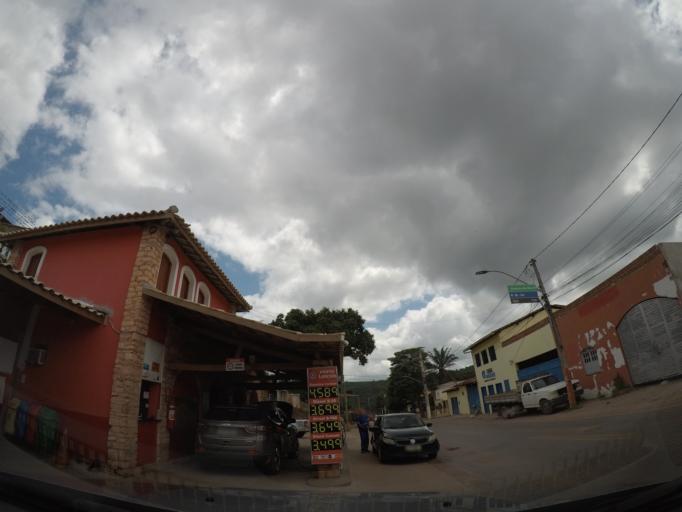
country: BR
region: Bahia
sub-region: Andarai
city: Vera Cruz
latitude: -12.5606
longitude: -41.3864
